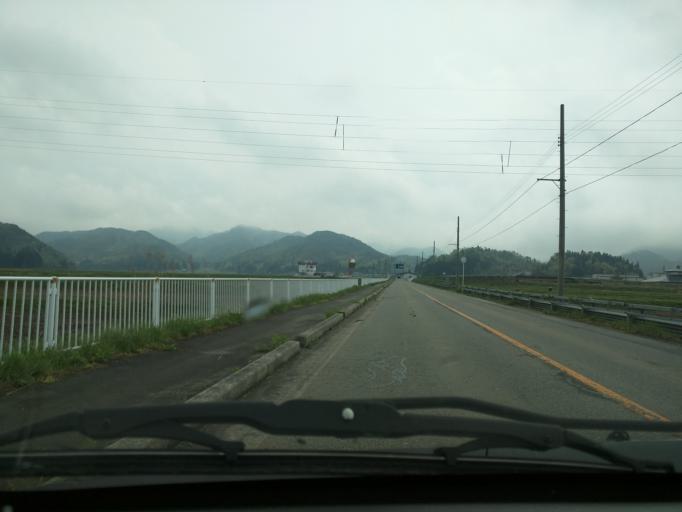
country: JP
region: Fukushima
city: Kitakata
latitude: 37.4388
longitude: 139.8813
